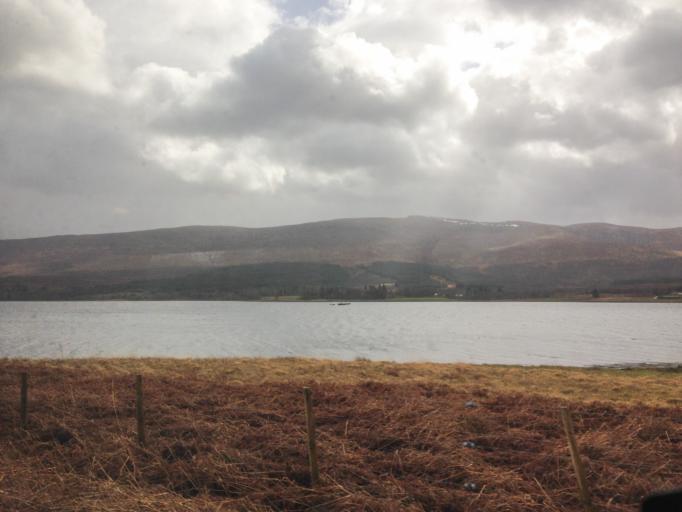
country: GB
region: Scotland
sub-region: Highland
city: Fort William
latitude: 56.8548
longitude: -5.2674
